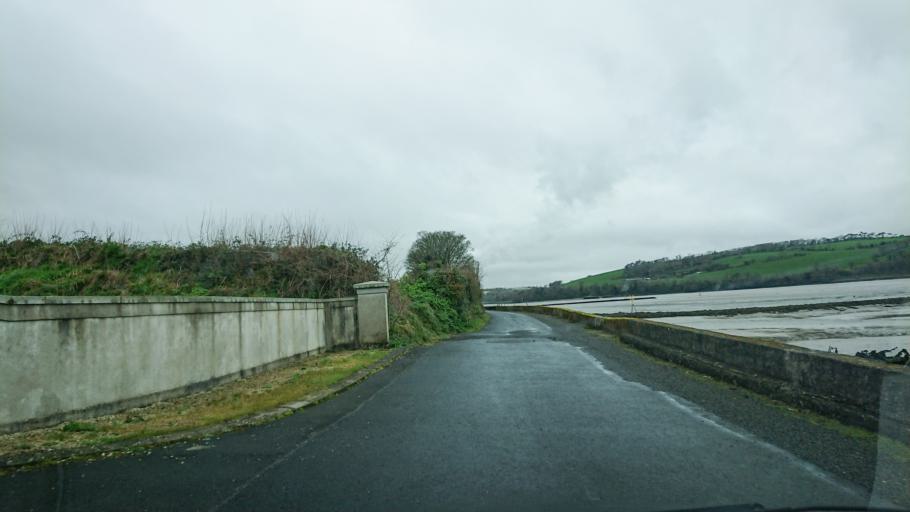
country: IE
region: Munster
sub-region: Waterford
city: Waterford
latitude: 52.2717
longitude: -6.9982
